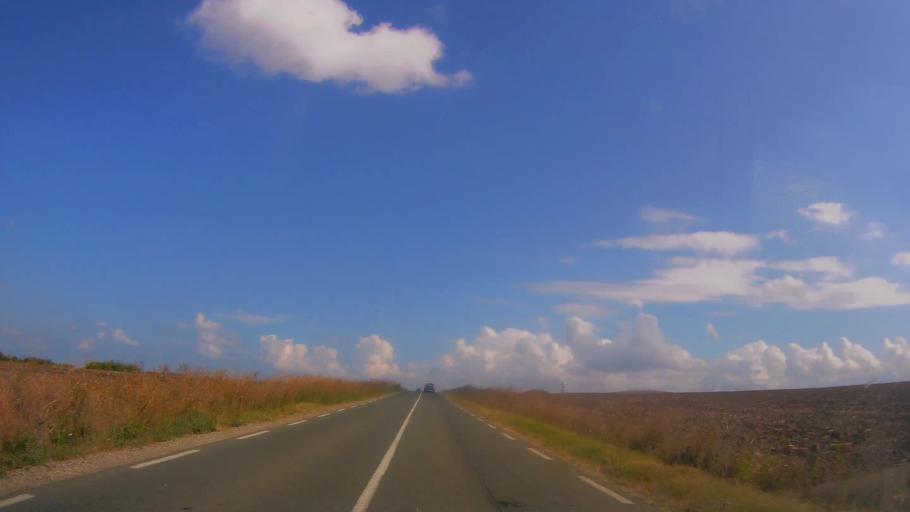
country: BG
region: Burgas
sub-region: Obshtina Kameno
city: Kameno
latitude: 42.4781
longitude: 27.3504
